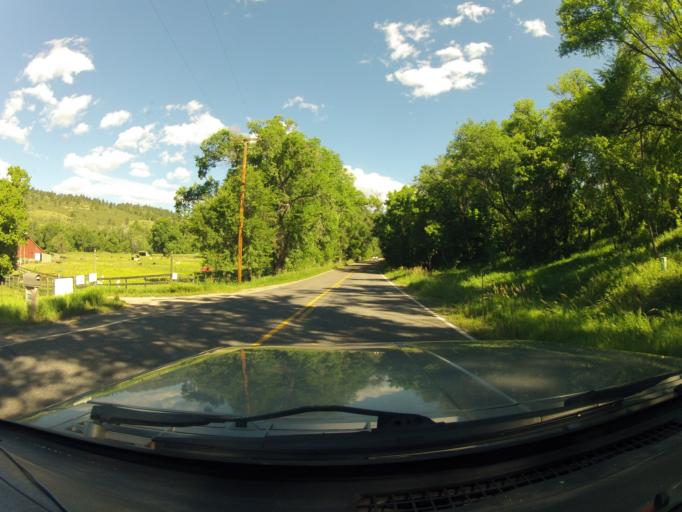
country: US
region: Colorado
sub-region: Larimer County
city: Laporte
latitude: 40.4885
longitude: -105.2163
